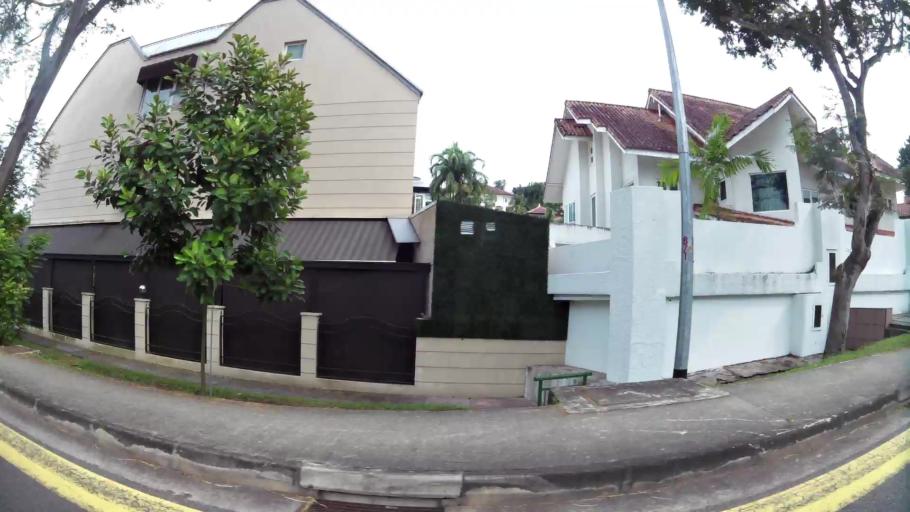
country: SG
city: Singapore
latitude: 1.3282
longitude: 103.7941
